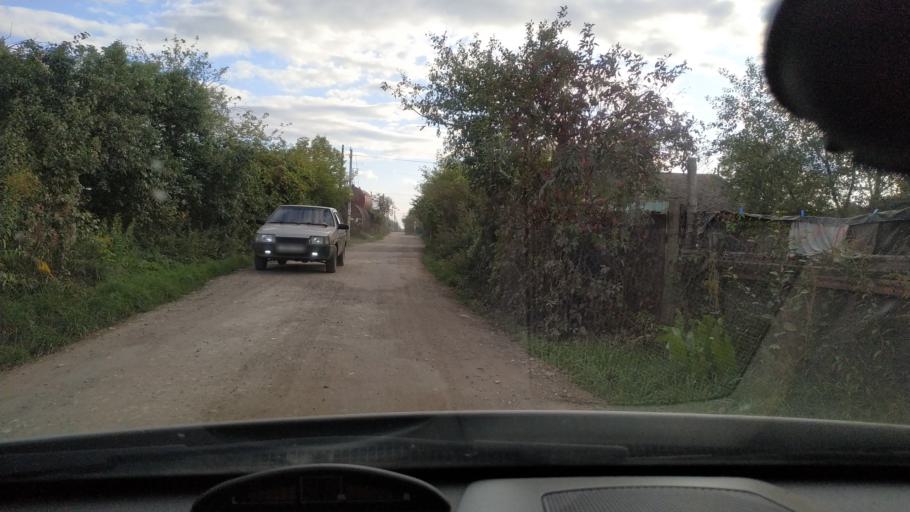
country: RU
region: Rjazan
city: Polyany
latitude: 54.5565
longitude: 39.8750
